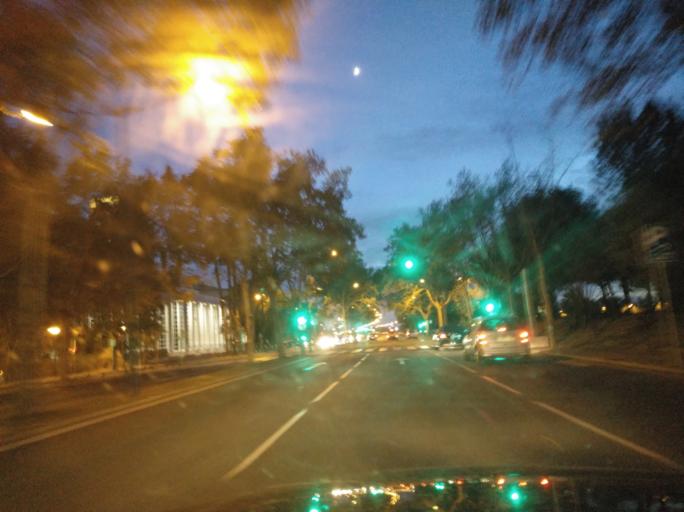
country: ES
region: Andalusia
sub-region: Provincia de Sevilla
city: Camas
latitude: 37.3968
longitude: -6.0124
